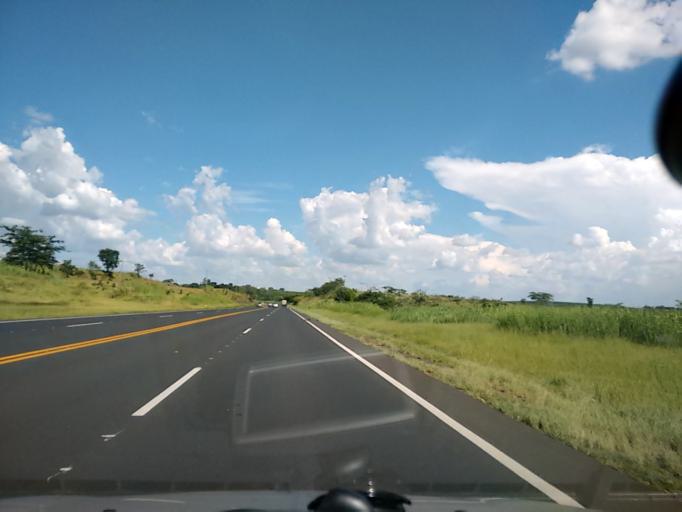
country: BR
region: Sao Paulo
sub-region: Pompeia
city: Pompeia
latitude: -22.1206
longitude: -50.1496
